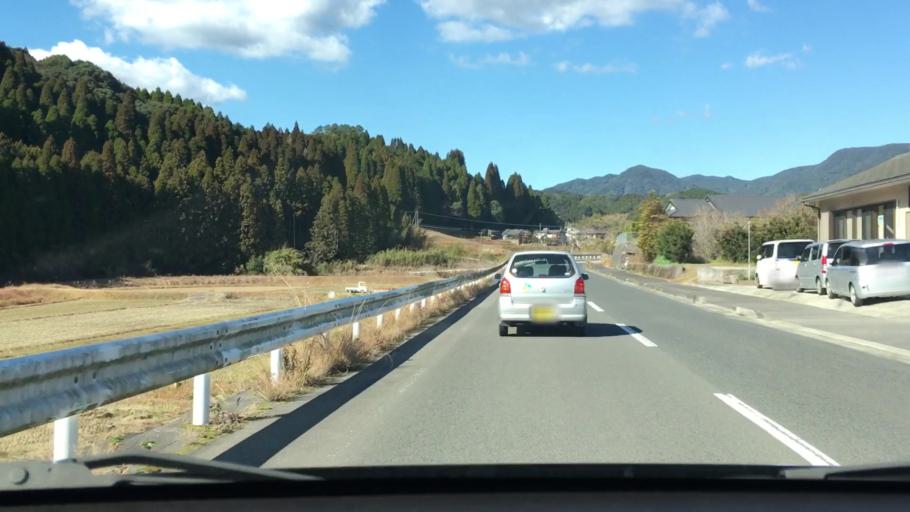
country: JP
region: Kagoshima
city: Ijuin
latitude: 31.6929
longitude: 130.4628
